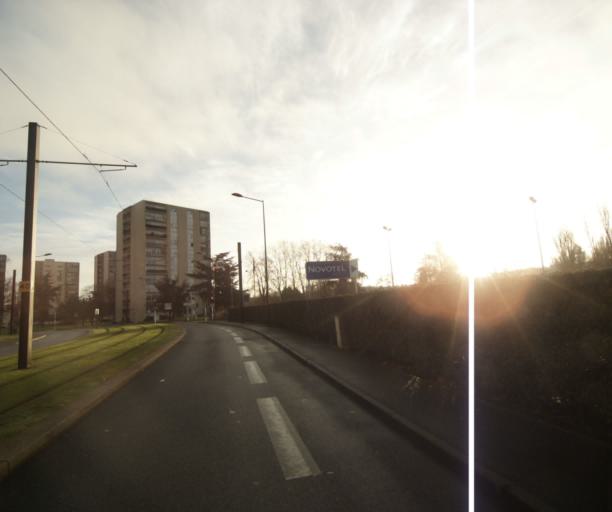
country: FR
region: Pays de la Loire
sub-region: Departement de la Sarthe
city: Le Mans
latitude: 47.9907
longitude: 0.2314
